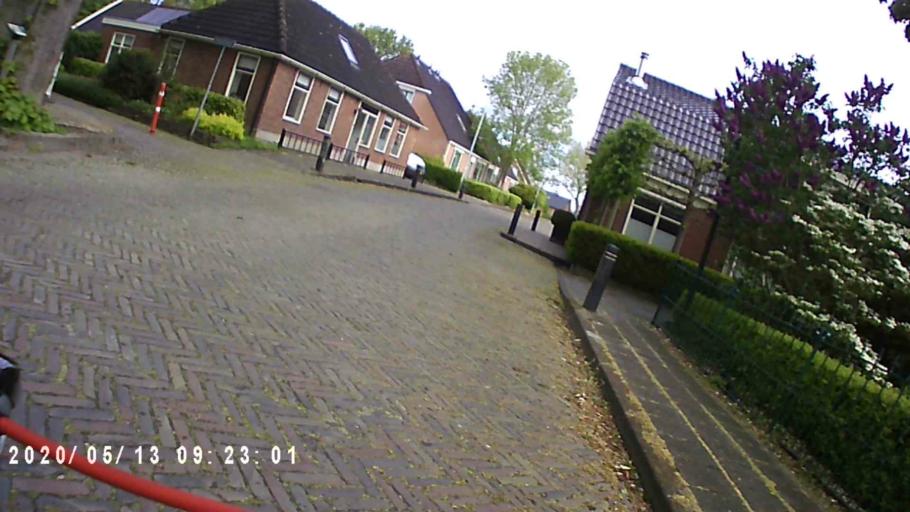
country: NL
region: Groningen
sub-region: Gemeente Zuidhorn
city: Noordhorn
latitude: 53.2611
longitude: 6.3965
